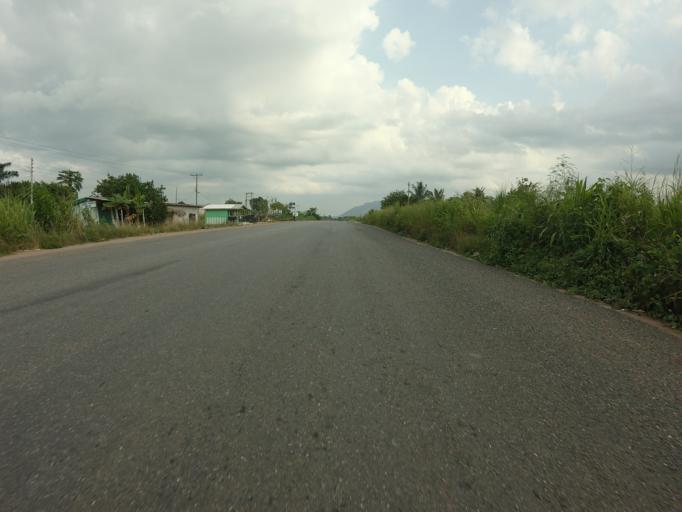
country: GH
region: Volta
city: Ho
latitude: 6.5762
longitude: 0.4834
